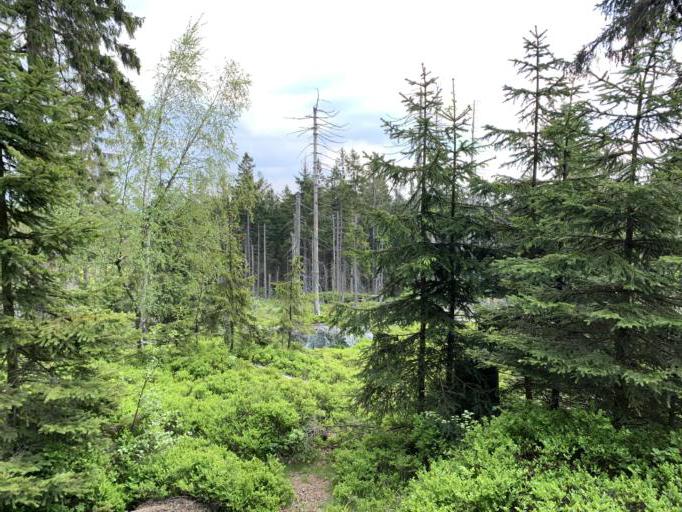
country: PL
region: Lower Silesian Voivodeship
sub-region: Powiat klodzki
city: Duszniki-Zdroj
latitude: 50.4568
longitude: 16.3509
